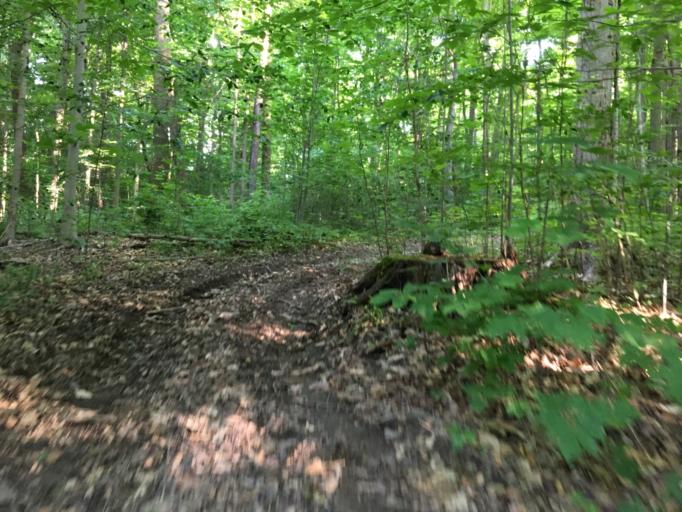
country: US
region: Ohio
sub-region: Geauga County
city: Middlefield
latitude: 41.4003
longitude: -81.0134
